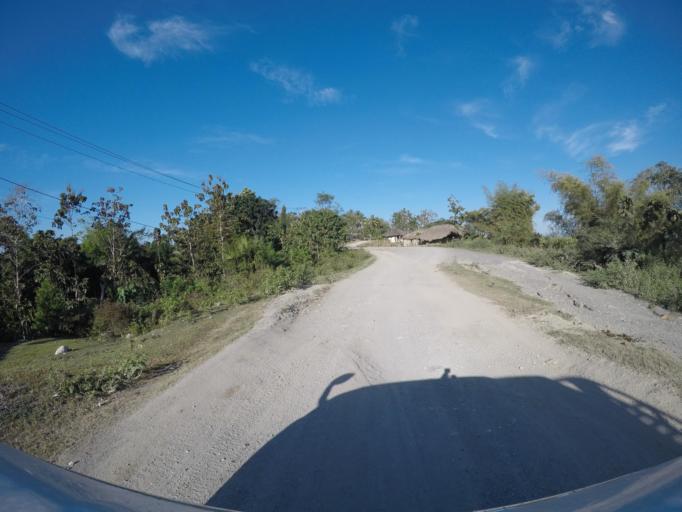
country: TL
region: Viqueque
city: Viqueque
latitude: -8.8701
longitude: 126.3282
